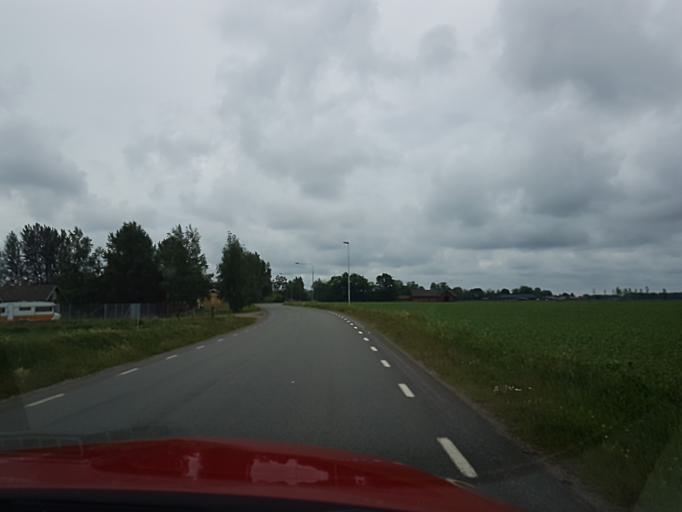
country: SE
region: Vaestra Goetaland
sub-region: Tidaholms Kommun
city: Olofstorp
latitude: 58.3420
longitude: 13.9707
